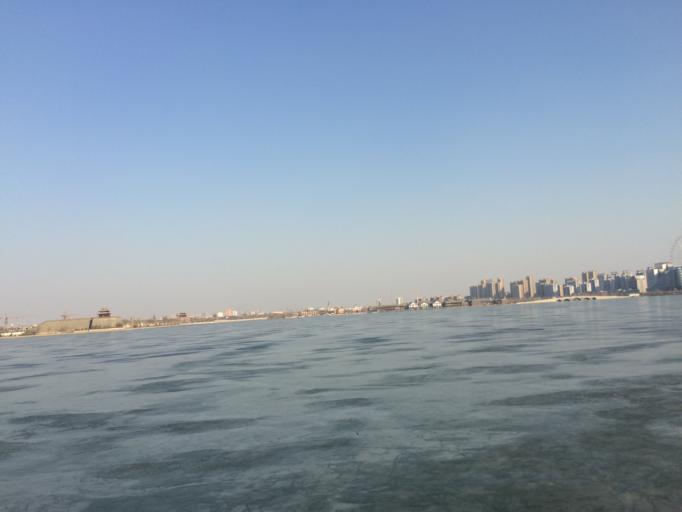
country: CN
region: Shandong Sheng
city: Gulou
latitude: 36.4378
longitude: 115.9515
